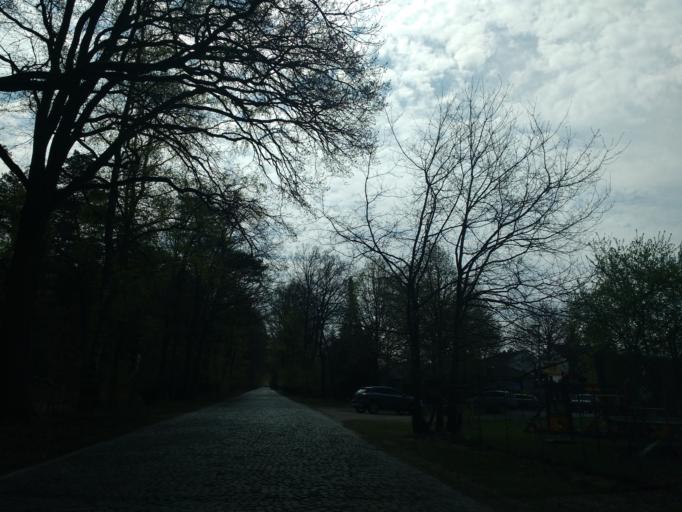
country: DE
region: North Rhine-Westphalia
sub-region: Regierungsbezirk Detmold
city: Paderborn
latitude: 51.7835
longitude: 8.7198
